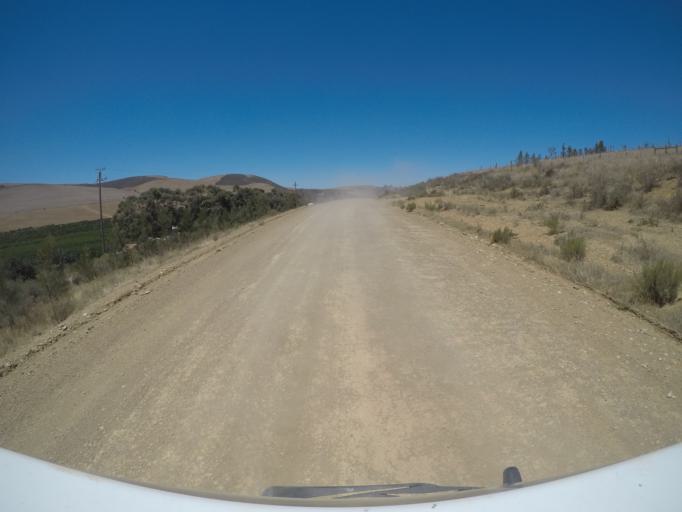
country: ZA
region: Western Cape
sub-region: Overberg District Municipality
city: Grabouw
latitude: -34.1041
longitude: 19.2086
